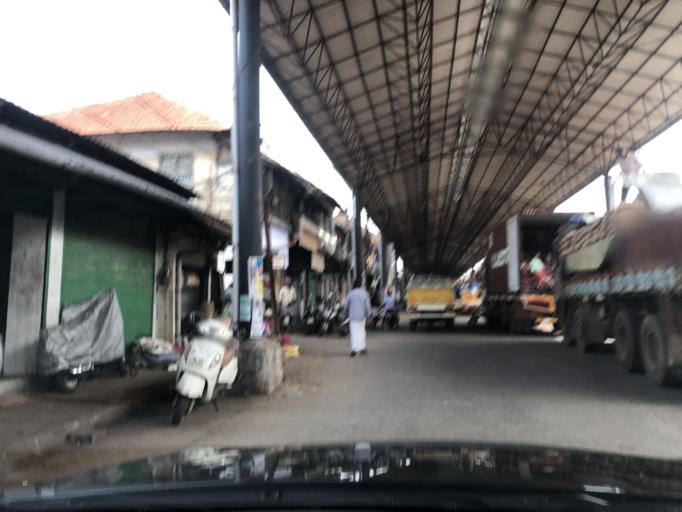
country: IN
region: Kerala
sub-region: Kozhikode
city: Kozhikode
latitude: 11.2490
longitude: 75.7746
